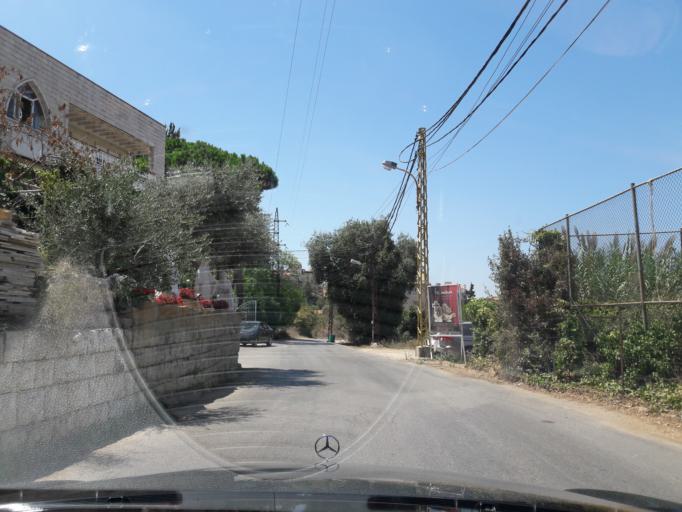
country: LB
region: Mont-Liban
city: Djounie
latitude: 33.9254
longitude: 35.6522
